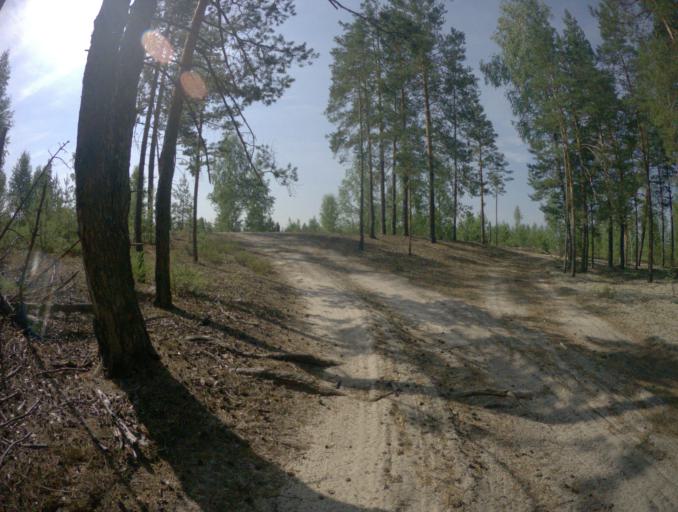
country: RU
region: Ivanovo
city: Talitsy
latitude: 56.4106
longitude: 42.2840
